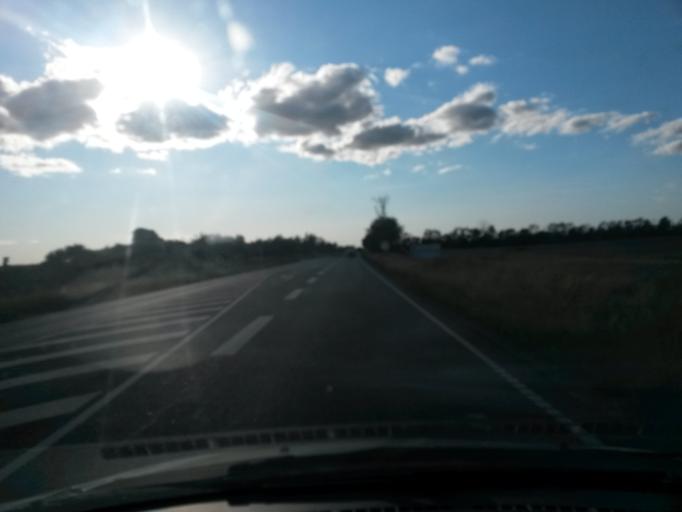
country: DK
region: Central Jutland
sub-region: Silkeborg Kommune
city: Kjellerup
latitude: 56.2995
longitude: 9.3319
